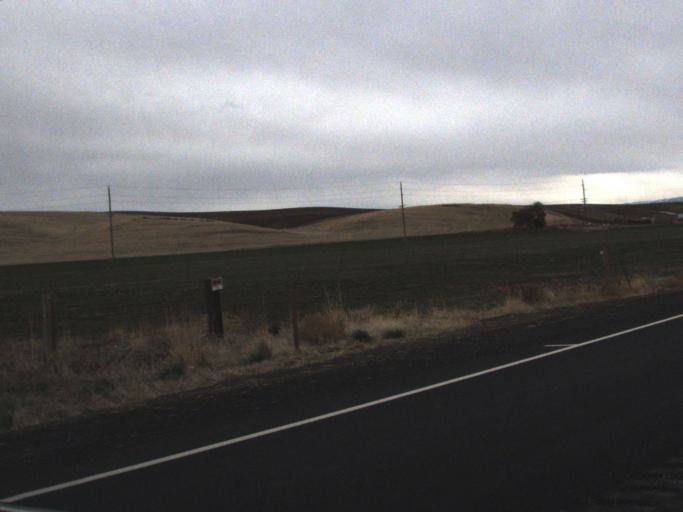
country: US
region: Washington
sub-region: Walla Walla County
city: Garrett
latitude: 46.0507
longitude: -118.5338
